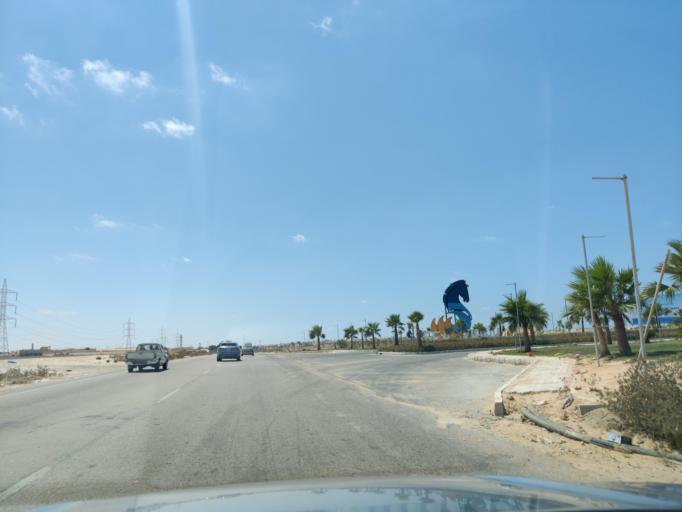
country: EG
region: Muhafazat Matruh
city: Al `Alamayn
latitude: 31.0685
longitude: 28.1689
